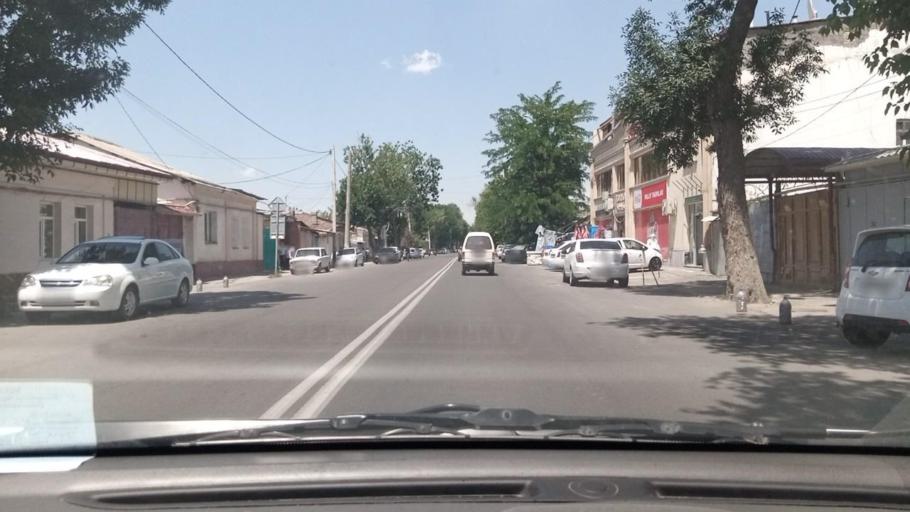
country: UZ
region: Toshkent Shahri
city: Tashkent
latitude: 41.2742
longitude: 69.2771
